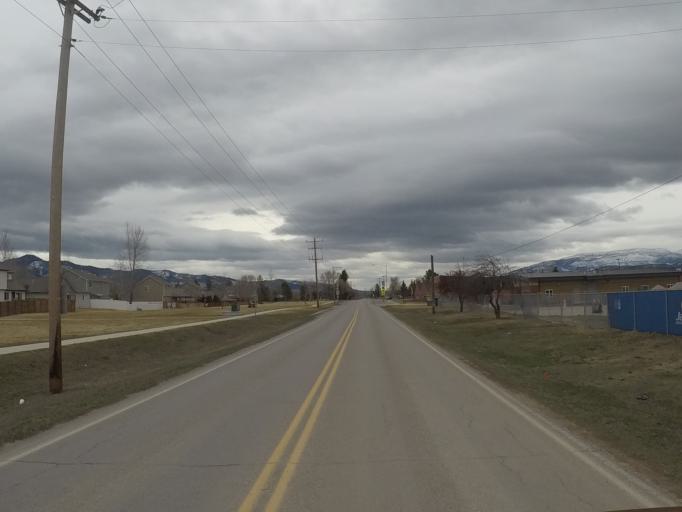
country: US
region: Montana
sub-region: Missoula County
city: Orchard Homes
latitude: 46.8948
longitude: -114.0553
